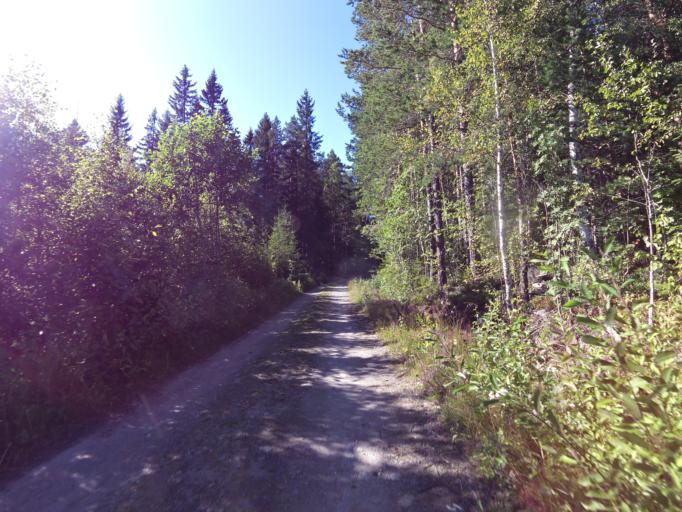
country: SE
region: Gaevleborg
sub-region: Hofors Kommun
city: Hofors
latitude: 60.5796
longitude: 16.4104
